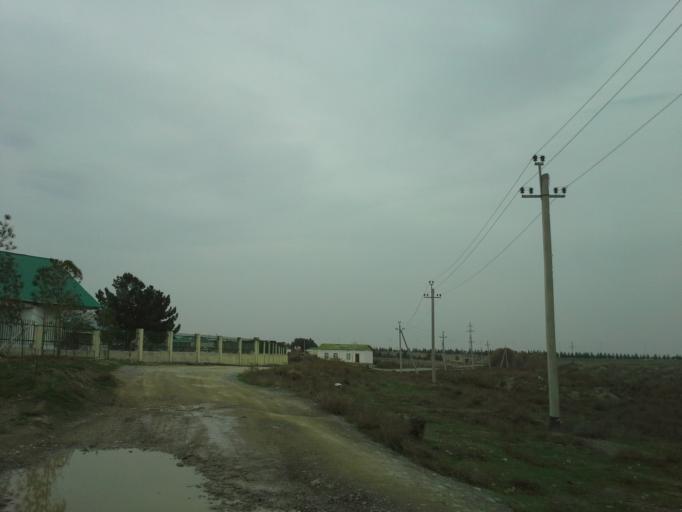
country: TM
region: Ahal
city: Abadan
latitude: 37.9782
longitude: 58.2269
